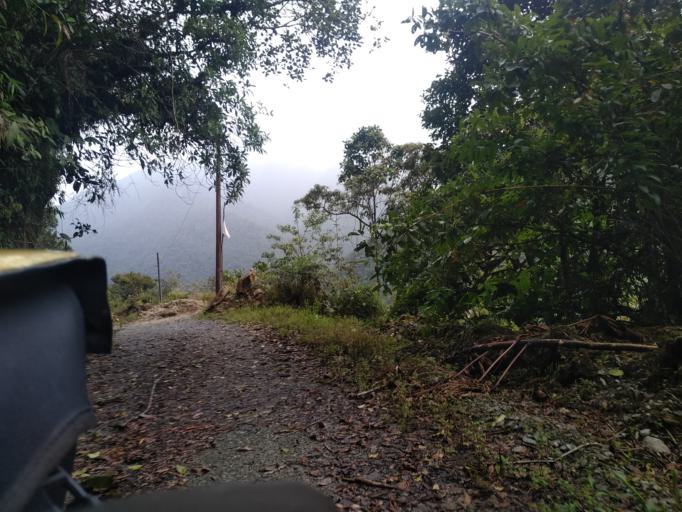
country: EC
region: Tungurahua
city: Banos
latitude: -1.4050
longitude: -78.2765
